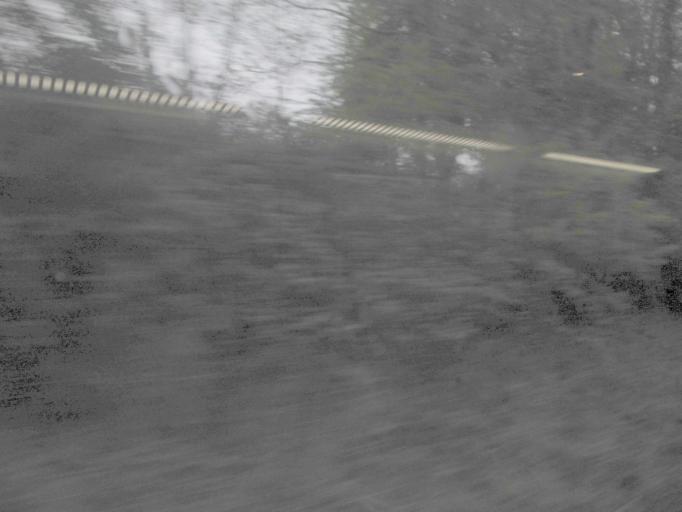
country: GB
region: England
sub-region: Wokingham
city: Winnersh
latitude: 51.4224
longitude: -0.8591
